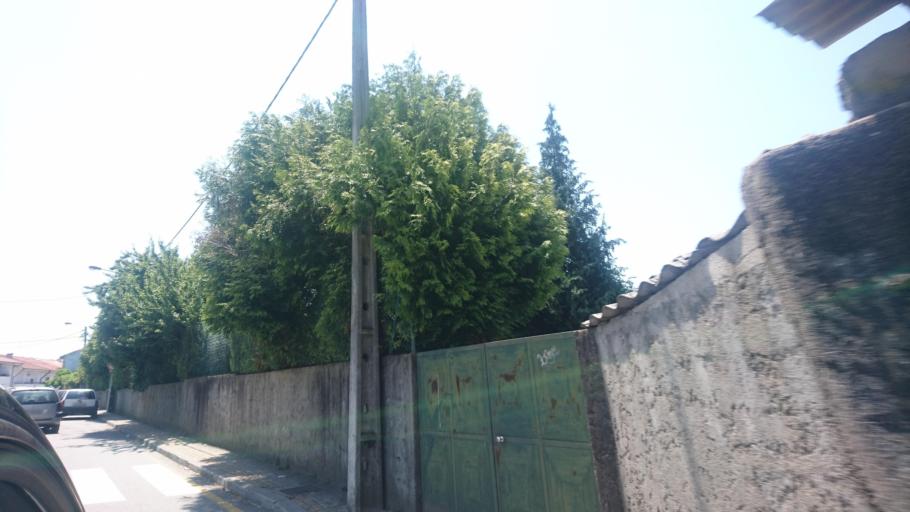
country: PT
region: Porto
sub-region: Gondomar
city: Rio Tinto
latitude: 41.1637
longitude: -8.5471
